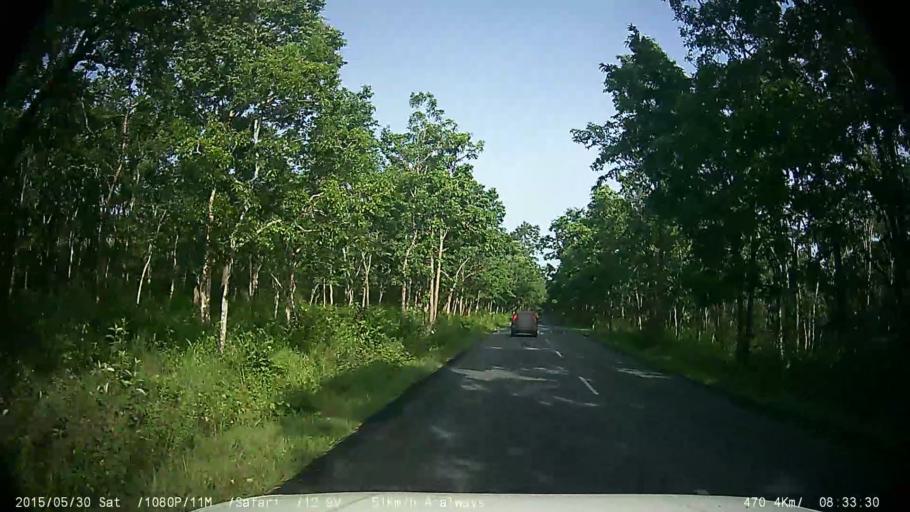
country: IN
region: Tamil Nadu
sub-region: Nilgiri
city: Masinigudi
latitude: 11.7282
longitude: 76.4476
